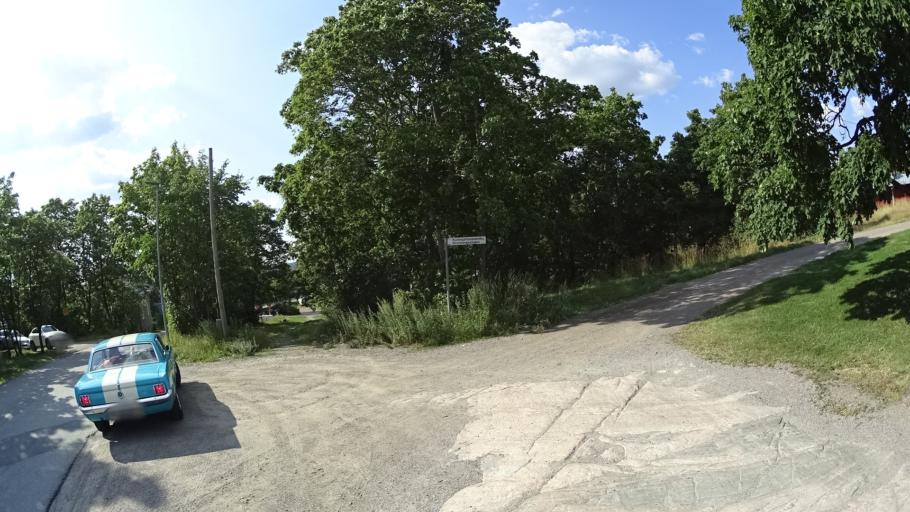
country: FI
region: Uusimaa
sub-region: Porvoo
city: Porvoo
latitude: 60.3991
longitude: 25.6618
